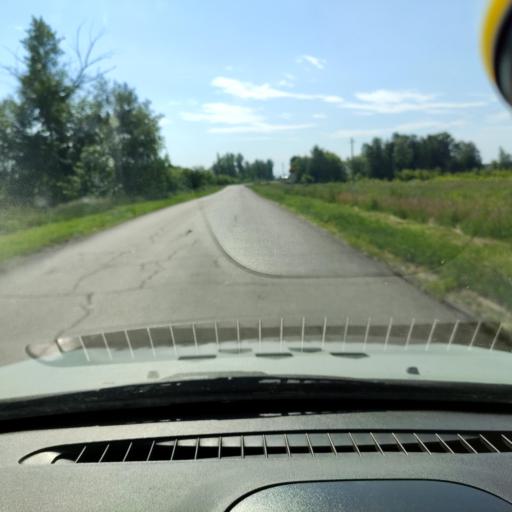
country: RU
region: Samara
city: Zhigulevsk
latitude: 53.3535
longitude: 49.3298
